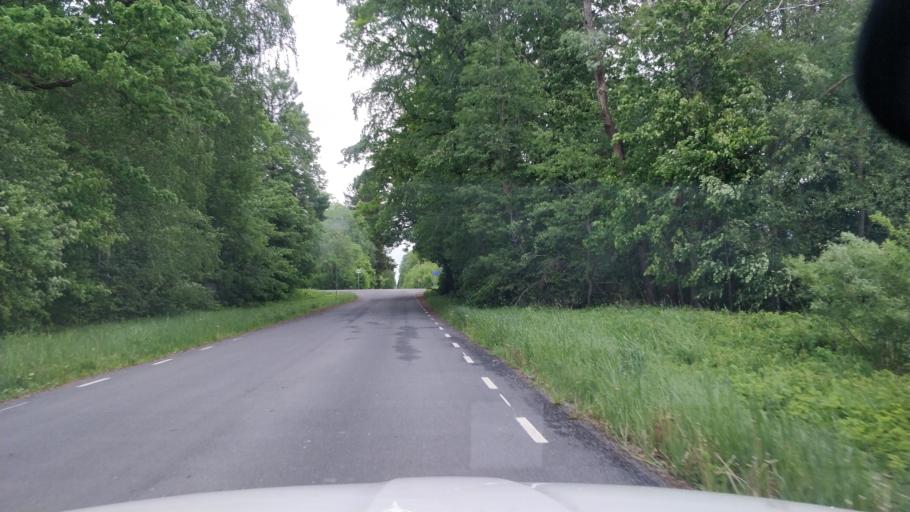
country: EE
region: Raplamaa
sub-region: Maerjamaa vald
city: Marjamaa
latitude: 58.7614
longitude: 24.2575
